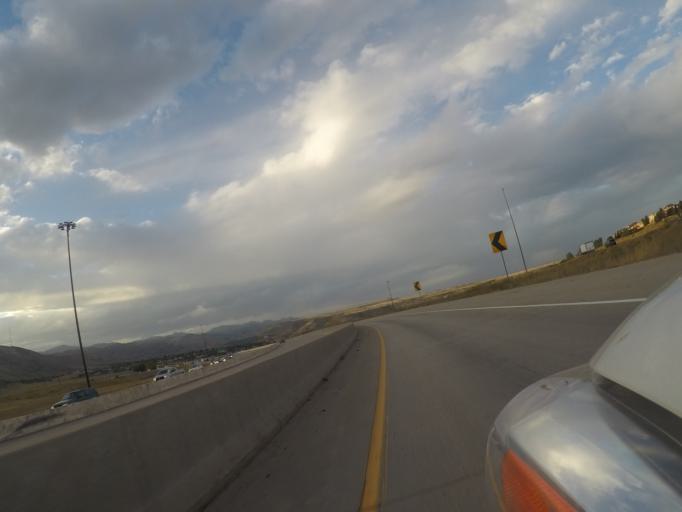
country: US
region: Colorado
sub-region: Jefferson County
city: West Pleasant View
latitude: 39.7095
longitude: -105.1921
